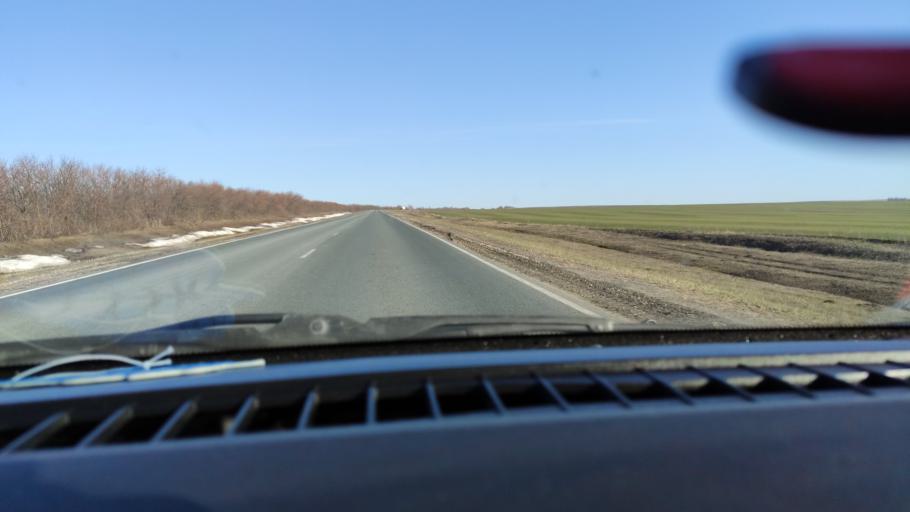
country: RU
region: Saratov
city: Dukhovnitskoye
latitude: 52.7617
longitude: 48.2407
